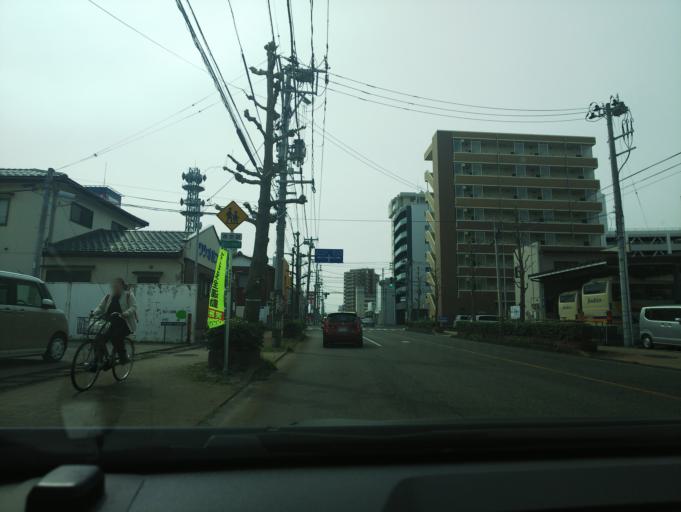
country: JP
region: Niigata
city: Niigata-shi
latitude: 37.9110
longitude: 139.0681
